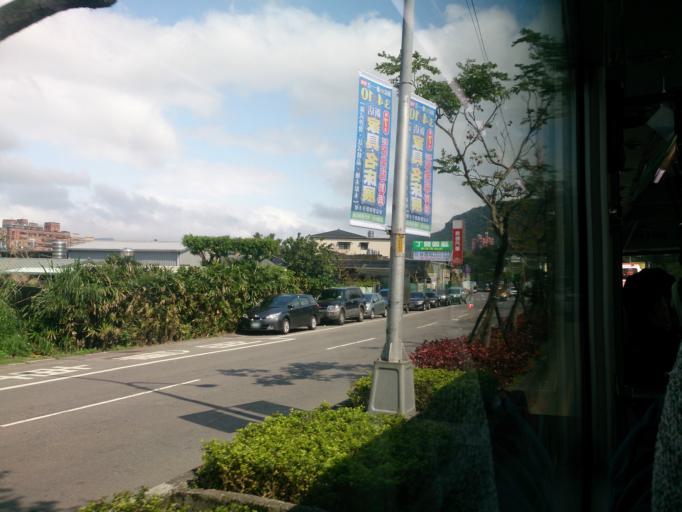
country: TW
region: Taipei
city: Taipei
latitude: 24.9982
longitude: 121.6115
